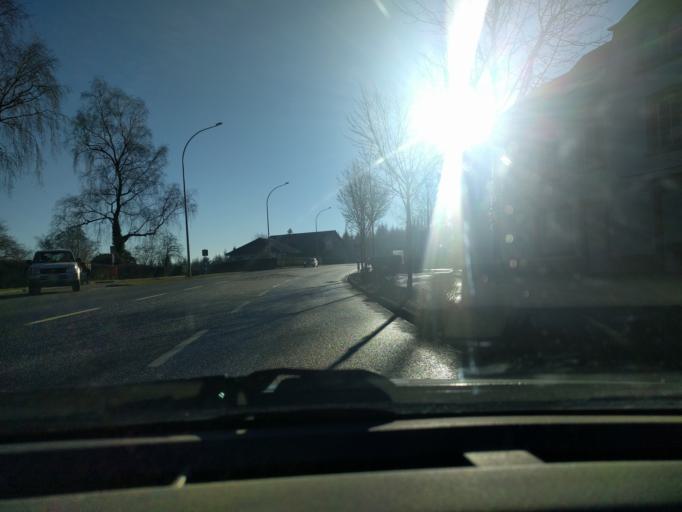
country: LU
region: Diekirch
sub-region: Canton de Clervaux
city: Troisvierges
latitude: 50.1809
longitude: 6.0240
